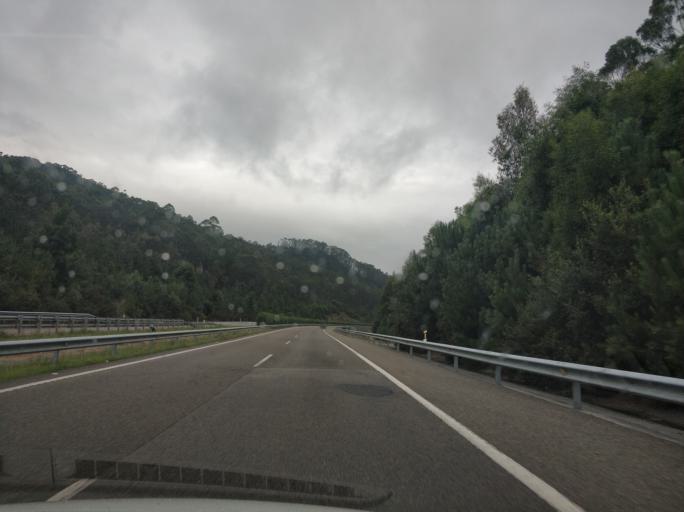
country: ES
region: Galicia
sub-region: Provincia de Lugo
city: Ribadeo
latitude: 43.5350
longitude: -7.1184
